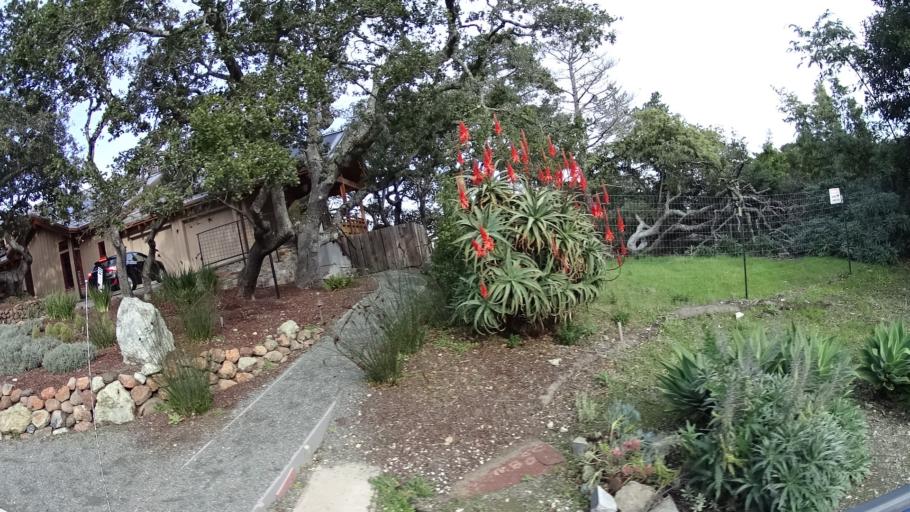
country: US
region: California
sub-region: San Mateo County
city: Hillsborough
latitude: 37.5552
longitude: -122.3627
